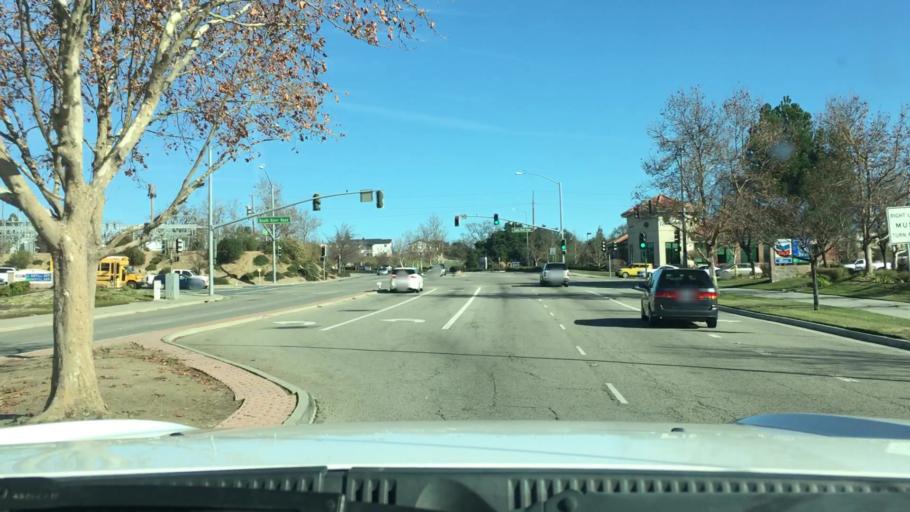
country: US
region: California
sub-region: San Luis Obispo County
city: Paso Robles
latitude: 35.6150
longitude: -120.6811
